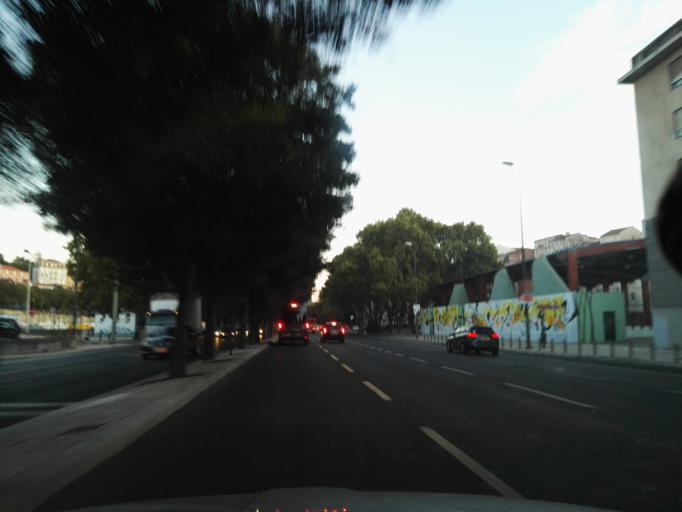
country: PT
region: Setubal
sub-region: Almada
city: Cacilhas
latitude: 38.7112
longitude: -9.1748
